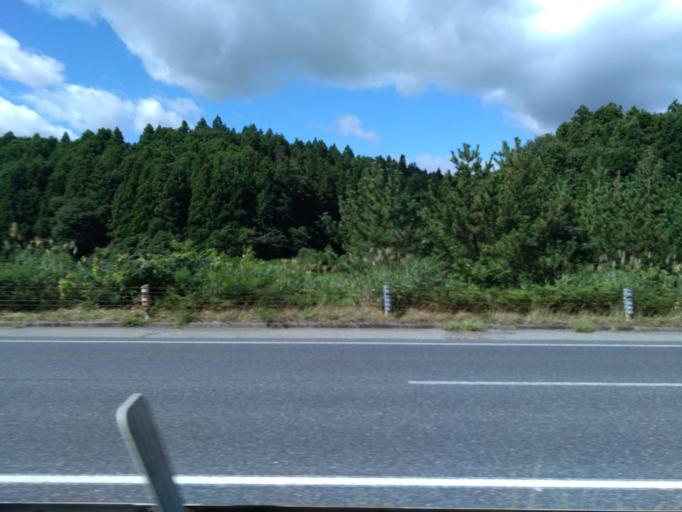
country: JP
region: Iwate
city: Ichinoseki
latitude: 38.8188
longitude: 141.0959
